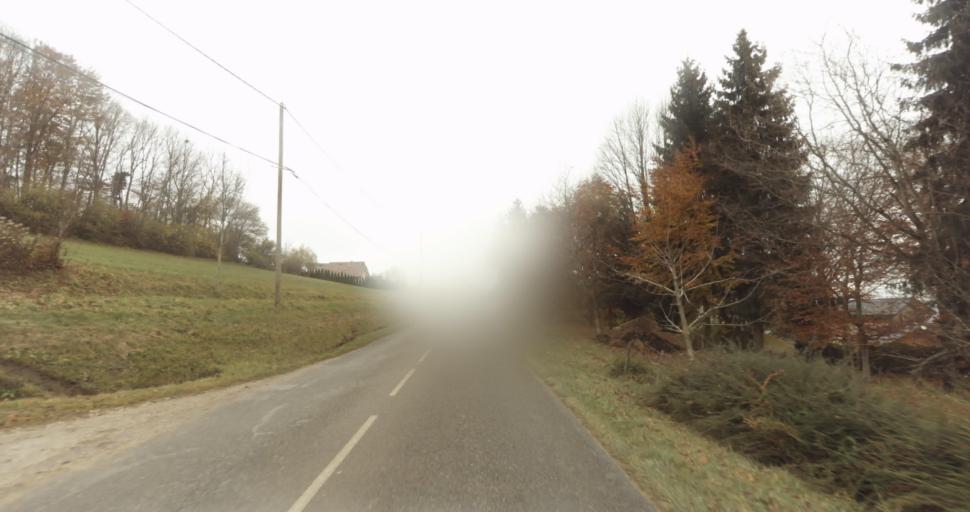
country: FR
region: Rhone-Alpes
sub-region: Departement de la Haute-Savoie
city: Thorens-Glieres
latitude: 46.0236
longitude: 6.2503
